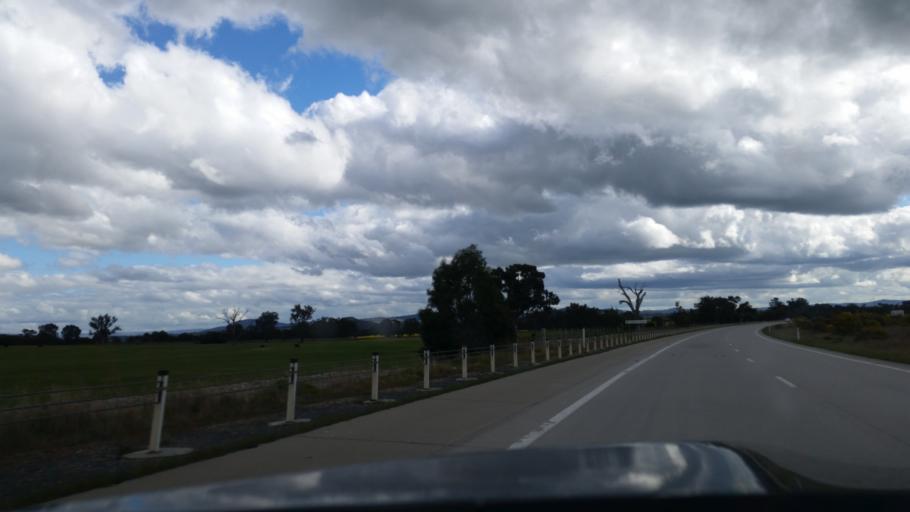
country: AU
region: New South Wales
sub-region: Albury Municipality
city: Lavington
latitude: -35.9271
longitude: 147.0835
